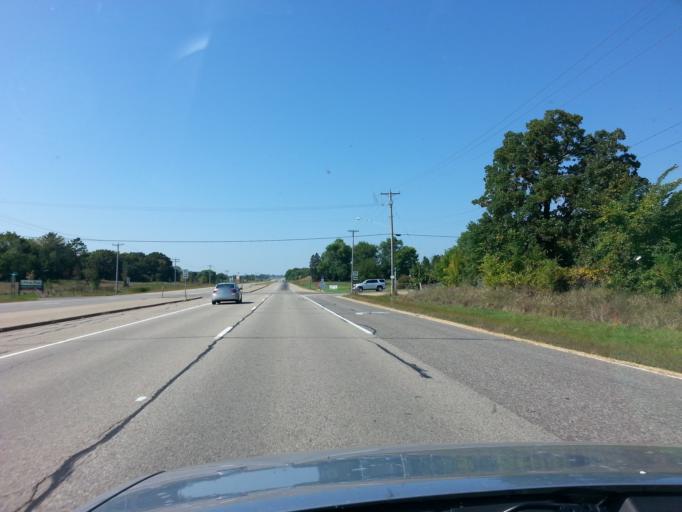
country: US
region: Minnesota
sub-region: Dakota County
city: Rosemount
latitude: 44.7390
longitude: -93.0537
